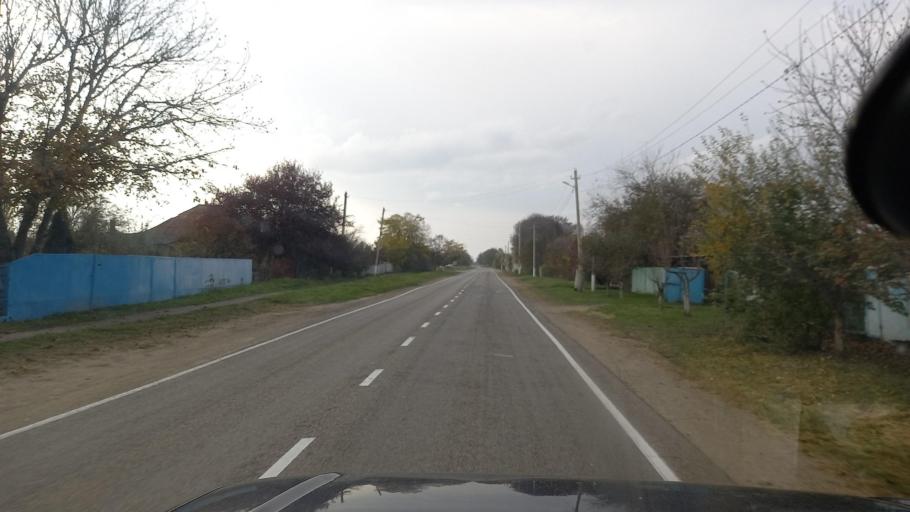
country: RU
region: Krasnodarskiy
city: Gubskaya
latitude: 44.3178
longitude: 40.6227
